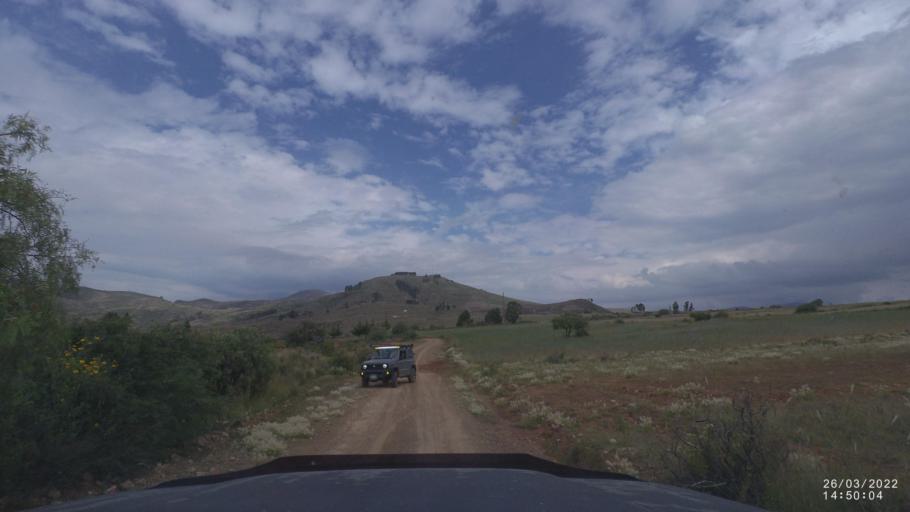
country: BO
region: Cochabamba
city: Cliza
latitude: -17.7270
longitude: -65.8500
